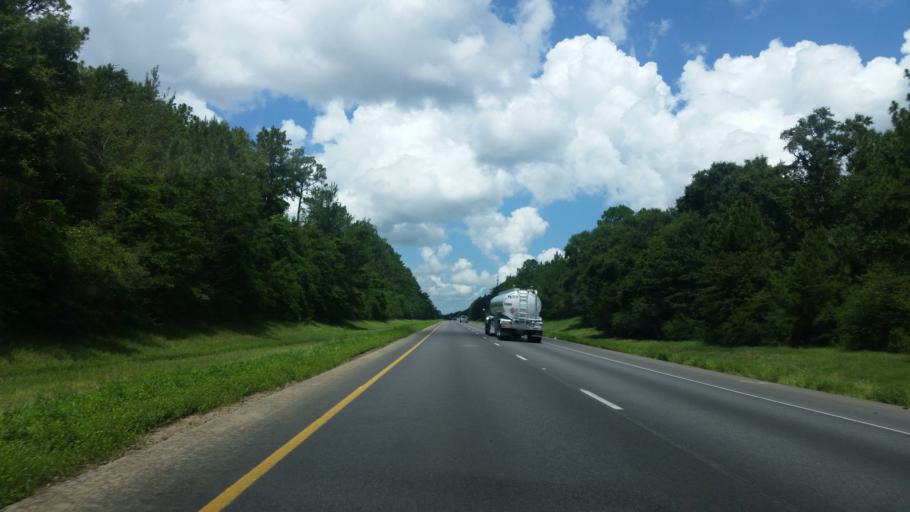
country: US
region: Alabama
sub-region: Baldwin County
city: Loxley
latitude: 30.6594
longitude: -87.8210
